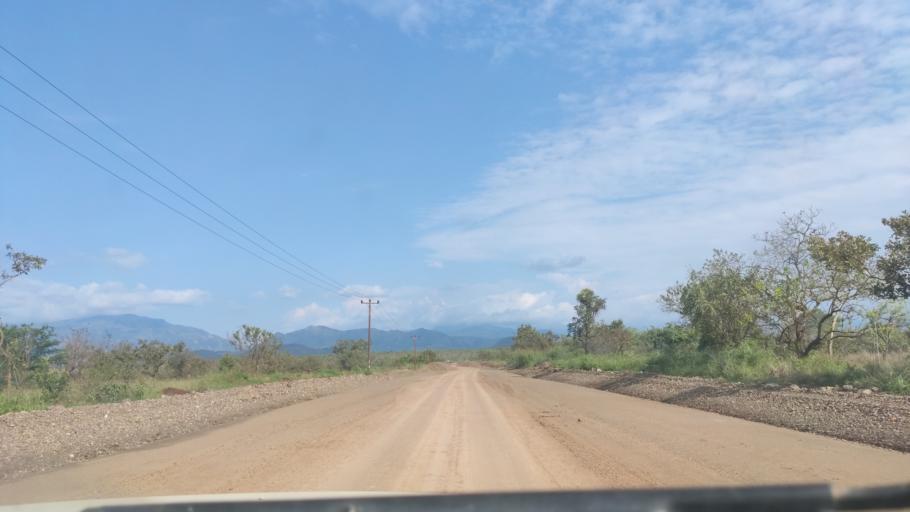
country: ET
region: Southern Nations, Nationalities, and People's Region
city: Felege Neway
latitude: 6.4256
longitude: 37.2314
